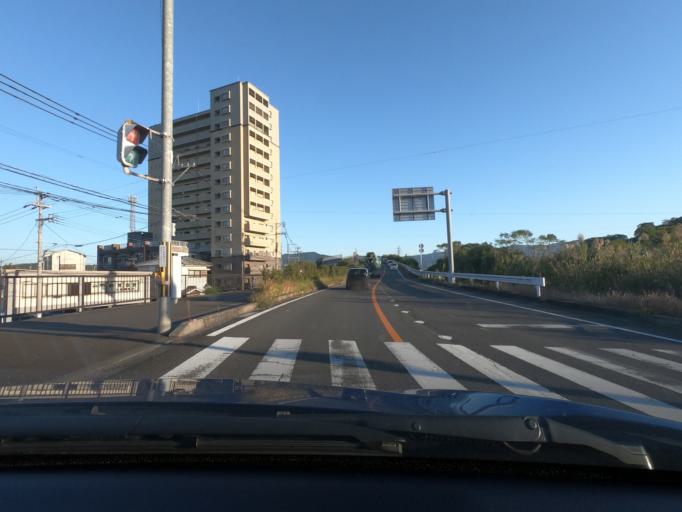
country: JP
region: Kagoshima
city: Satsumasendai
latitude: 31.8121
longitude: 130.3113
